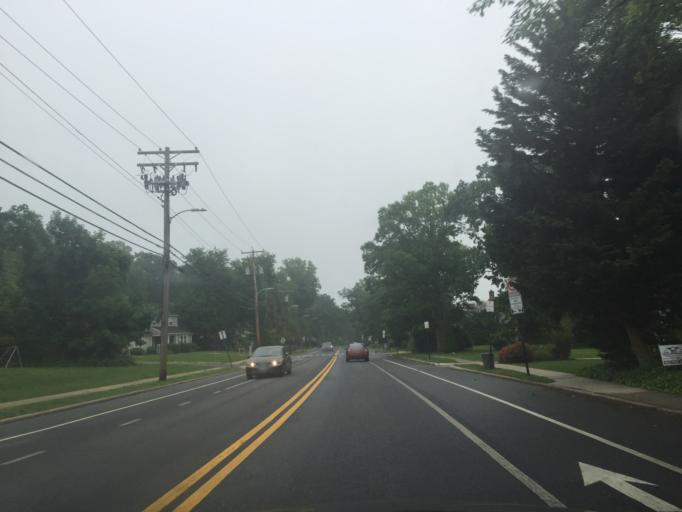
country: US
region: Maryland
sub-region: Baltimore County
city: Pikesville
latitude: 39.3675
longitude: -76.6788
